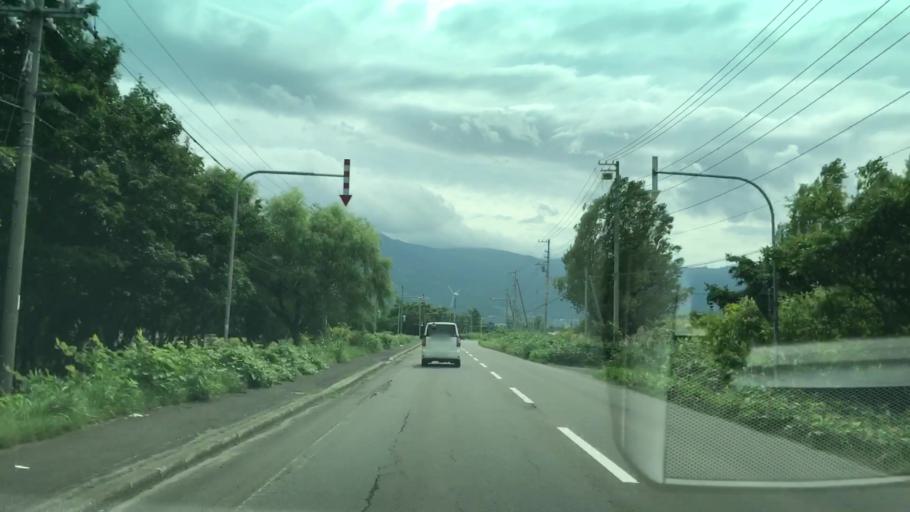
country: JP
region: Hokkaido
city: Iwanai
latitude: 43.0040
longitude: 140.5420
